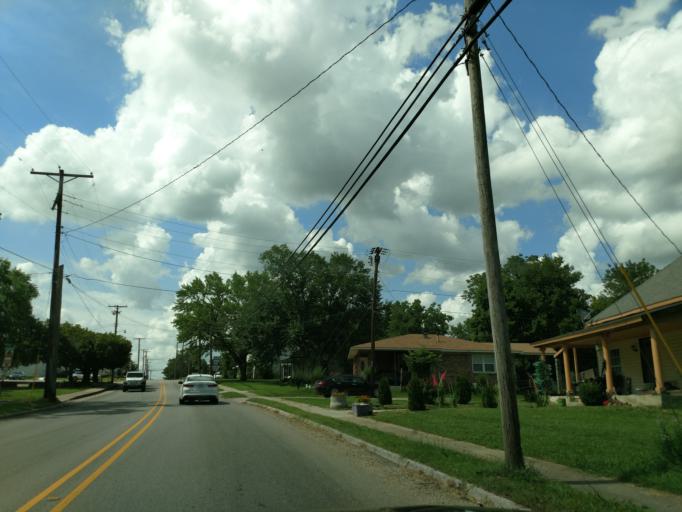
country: US
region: Arkansas
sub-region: Carroll County
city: Berryville
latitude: 36.3628
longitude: -93.5646
